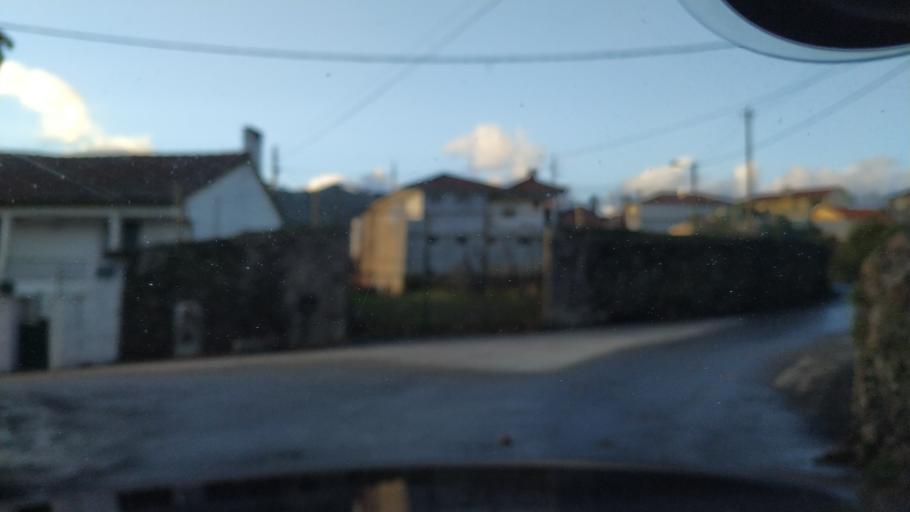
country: PT
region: Vila Real
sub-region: Vila Real
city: Vila Real
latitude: 41.2568
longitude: -7.7618
